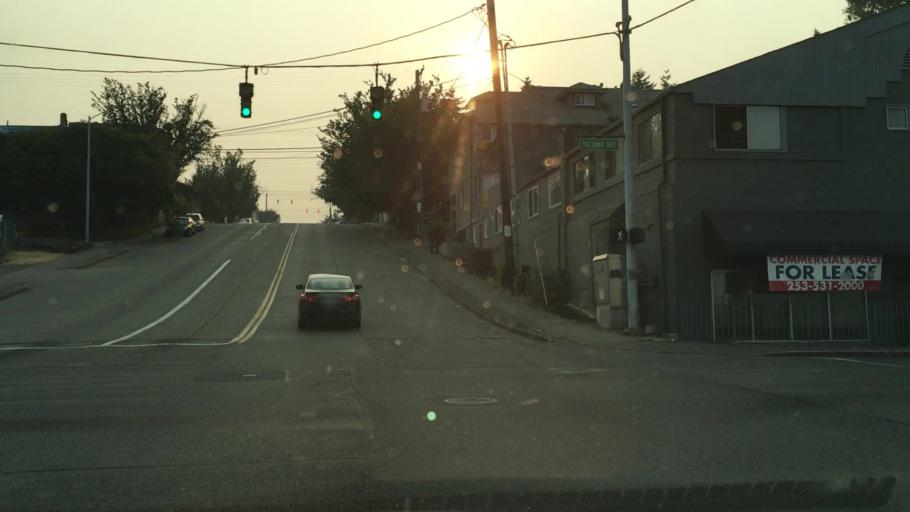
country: US
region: Washington
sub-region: Pierce County
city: Tacoma
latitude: 47.2487
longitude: -122.4435
